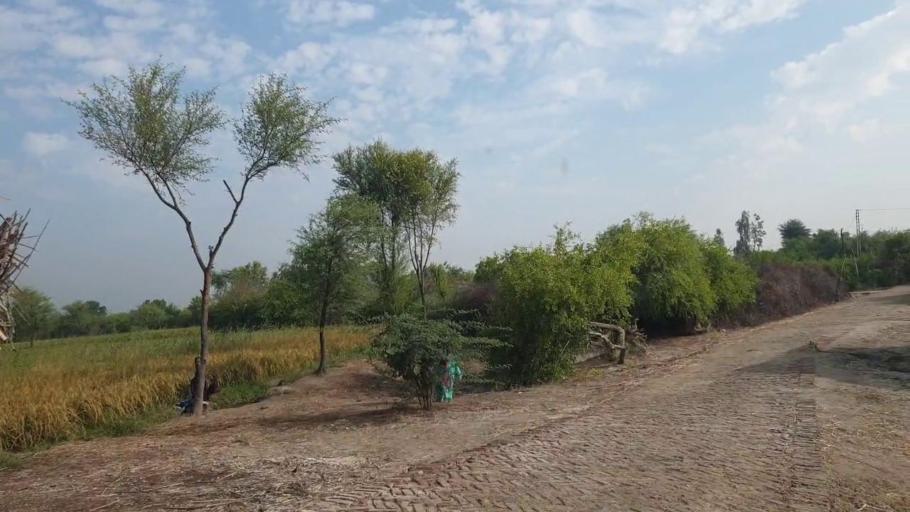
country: PK
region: Sindh
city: Tando Bago
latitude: 24.8576
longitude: 68.9868
